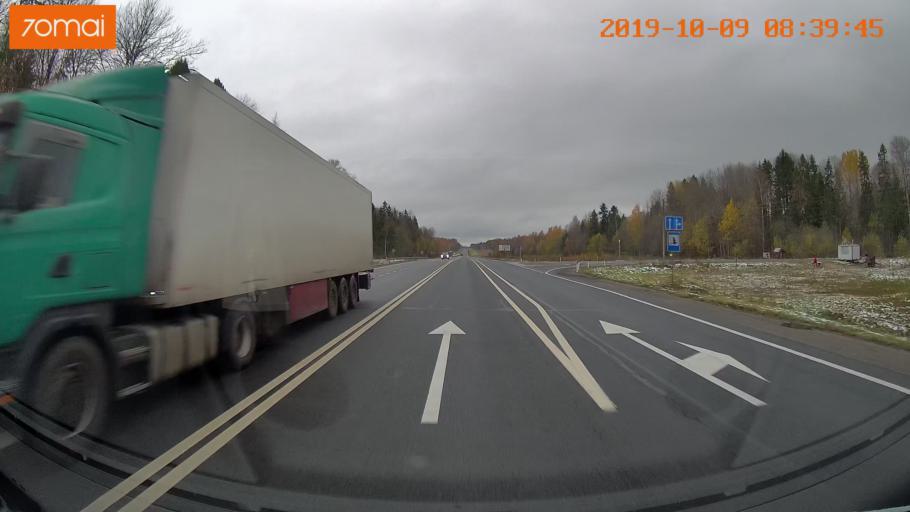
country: RU
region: Vologda
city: Gryazovets
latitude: 58.9763
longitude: 40.1491
